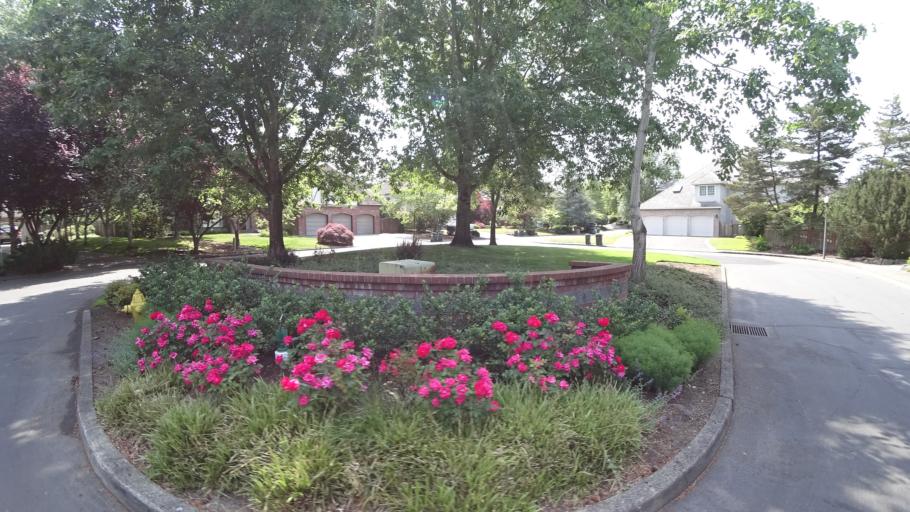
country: US
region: Oregon
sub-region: Washington County
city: Oak Hills
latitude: 45.5465
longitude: -122.8200
